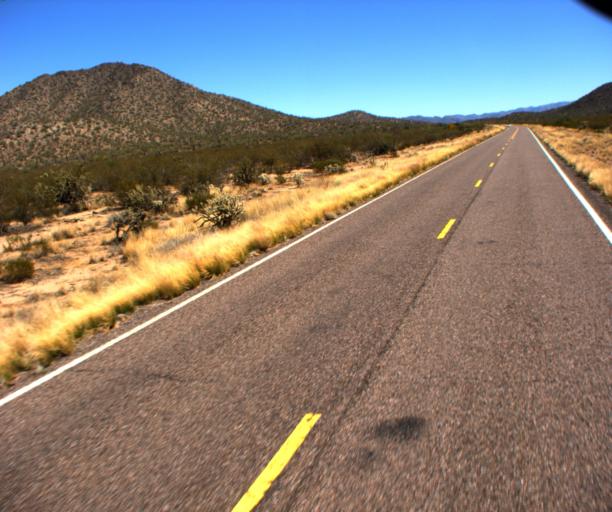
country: US
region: Arizona
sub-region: Yavapai County
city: Congress
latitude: 34.0913
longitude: -113.0070
